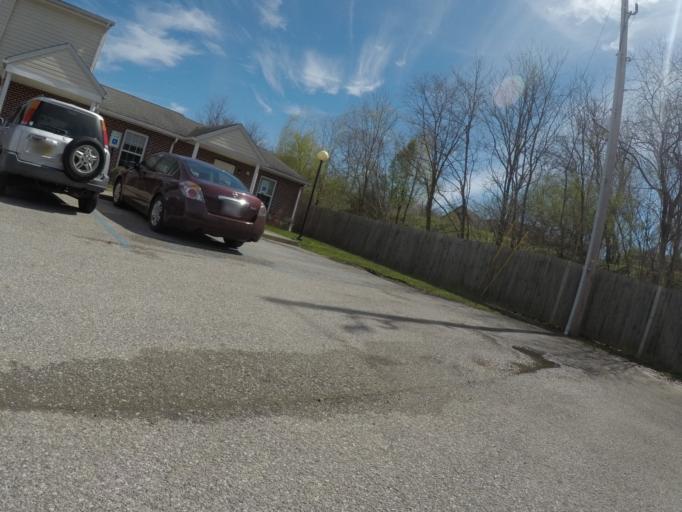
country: US
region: West Virginia
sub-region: Cabell County
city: Barboursville
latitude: 38.4096
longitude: -82.3076
